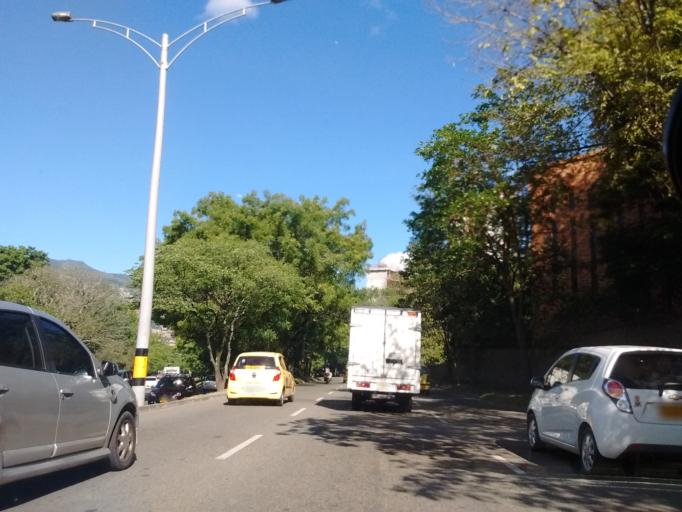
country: CO
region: Antioquia
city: Medellin
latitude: 6.2595
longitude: -75.5822
